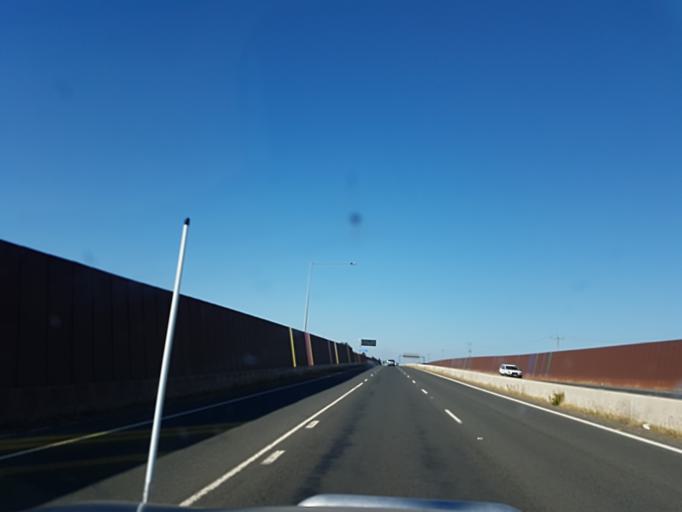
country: AU
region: Victoria
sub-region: Greater Geelong
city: Wandana Heights
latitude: -38.2136
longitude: 144.2927
